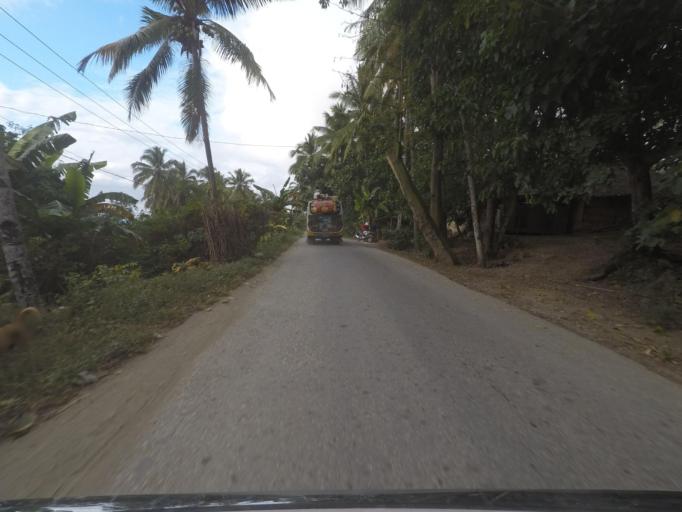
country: TL
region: Baucau
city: Baucau
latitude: -8.5160
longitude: 126.4390
